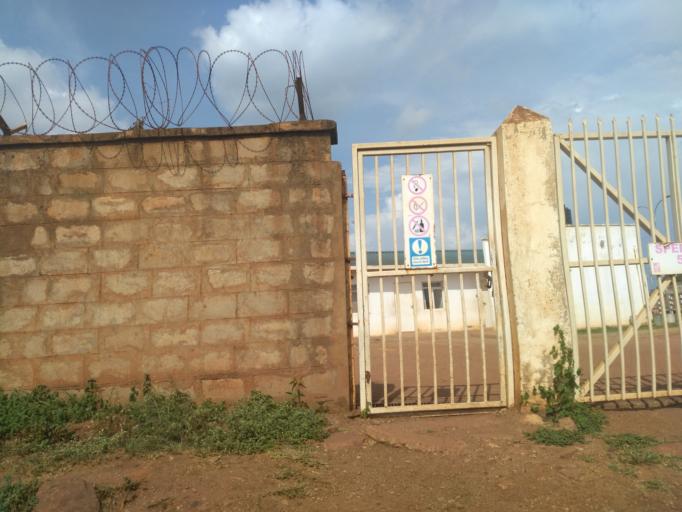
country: UG
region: Eastern Region
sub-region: Jinja District
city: Jinja
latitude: 0.4257
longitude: 33.2202
